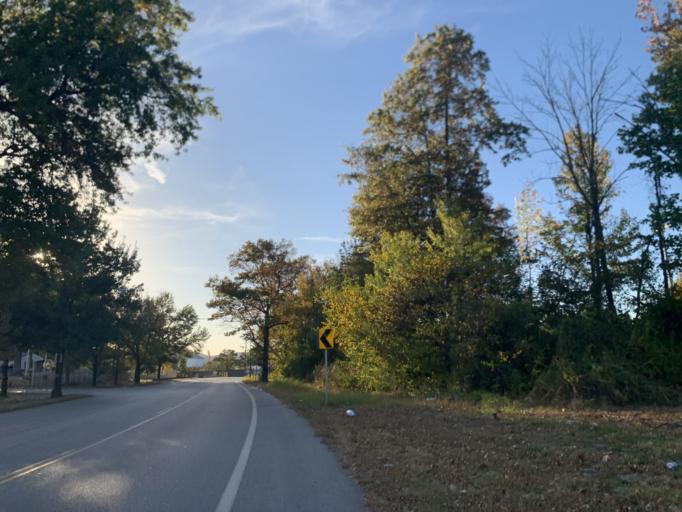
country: US
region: Kentucky
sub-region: Jefferson County
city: Shively
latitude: 38.2326
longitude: -85.8287
